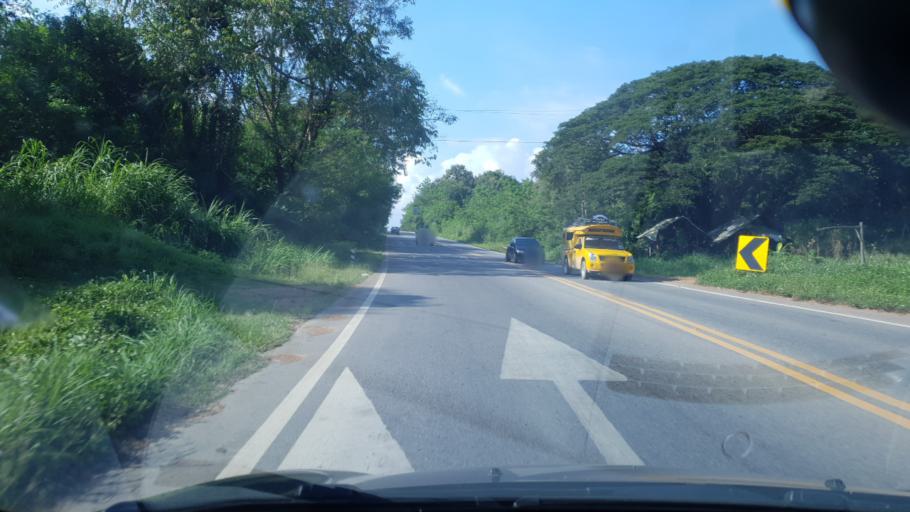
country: TH
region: Chiang Mai
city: Mae On
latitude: 18.9234
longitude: 99.2403
